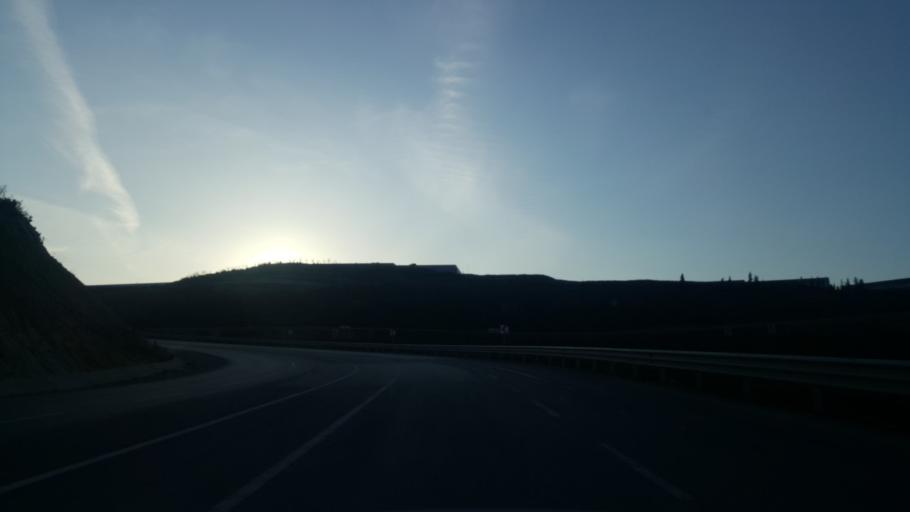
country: TR
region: Kocaeli
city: Tavsanli
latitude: 40.8416
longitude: 29.5487
